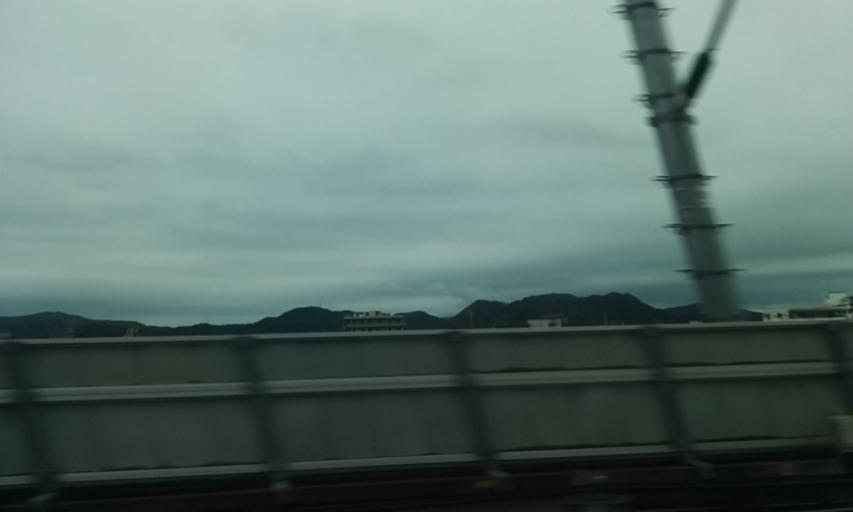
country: JP
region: Hyogo
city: Himeji
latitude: 34.8228
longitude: 134.7205
